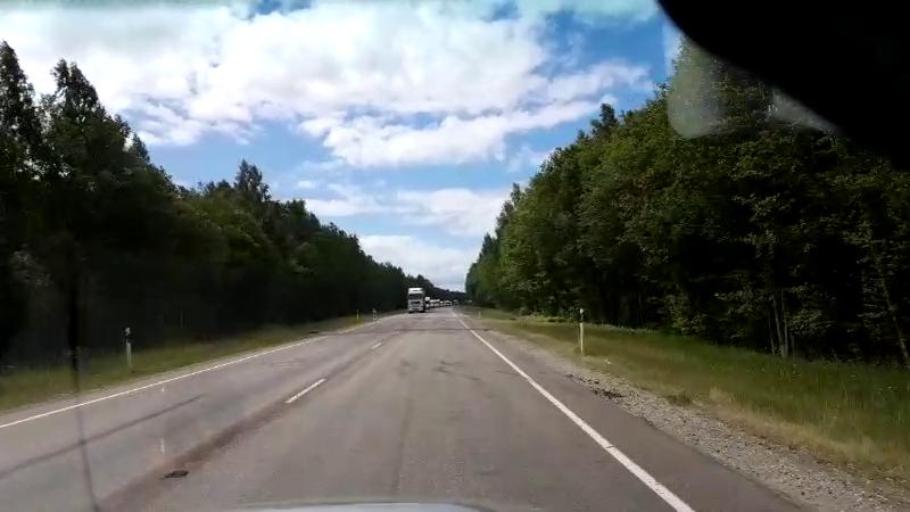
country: LV
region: Salacgrivas
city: Ainazi
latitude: 58.0184
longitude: 24.4973
